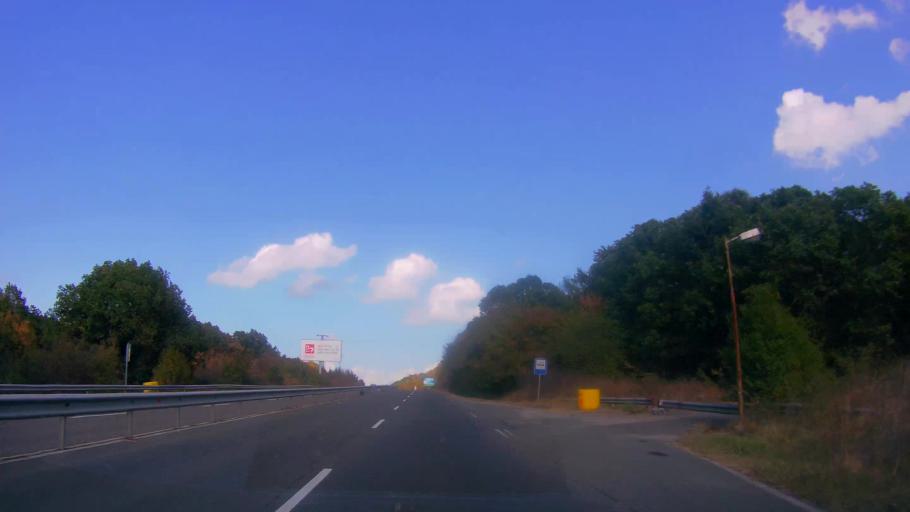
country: BG
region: Burgas
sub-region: Obshtina Sozopol
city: Chernomorets
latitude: 42.4332
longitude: 27.5576
